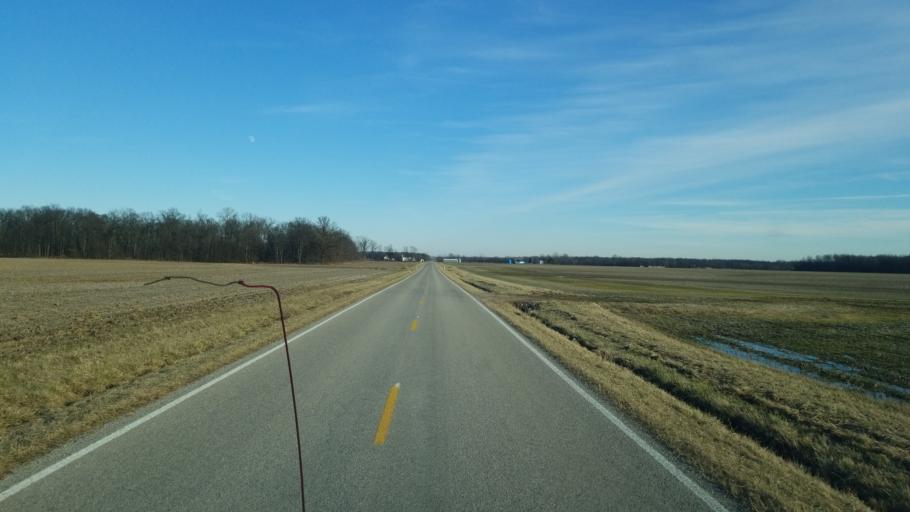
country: US
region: Ohio
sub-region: Huron County
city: Bellevue
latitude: 41.1798
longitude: -82.8029
